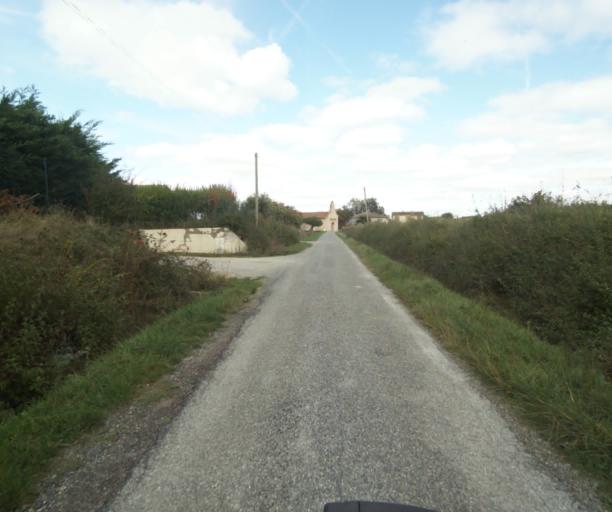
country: FR
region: Midi-Pyrenees
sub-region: Departement du Tarn-et-Garonne
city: Saint-Porquier
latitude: 43.9568
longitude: 1.1494
